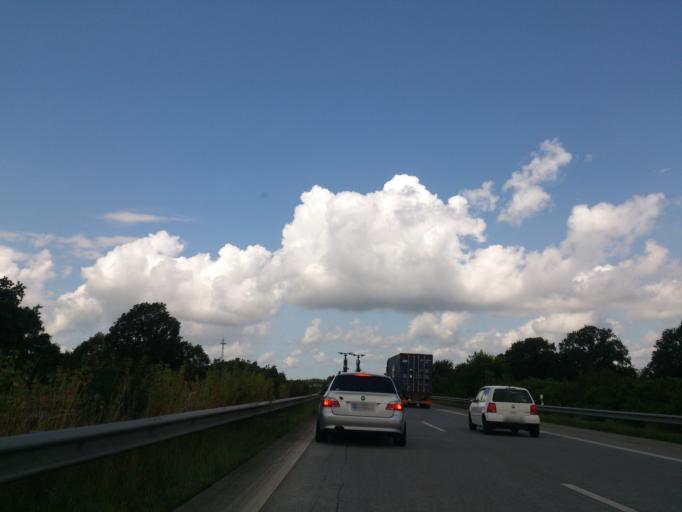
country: DE
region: Schleswig-Holstein
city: Dageling
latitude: 53.8843
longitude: 9.5432
